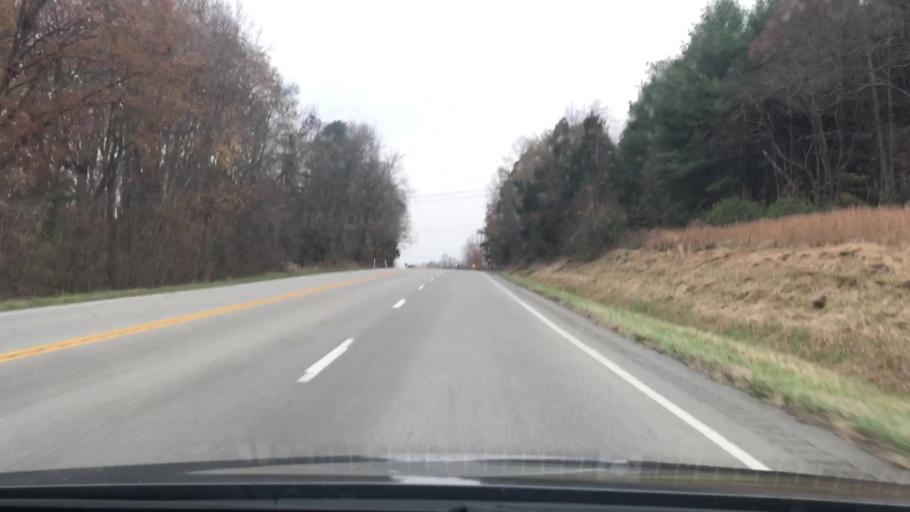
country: US
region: Kentucky
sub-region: Allen County
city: Scottsville
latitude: 36.8425
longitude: -86.0750
